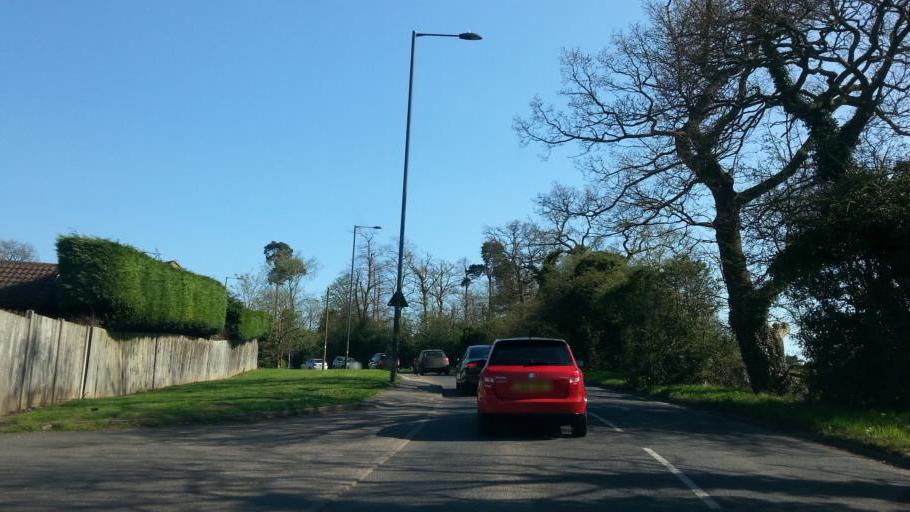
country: GB
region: England
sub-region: Worcestershire
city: Alvechurch
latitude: 52.3896
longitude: -1.9611
